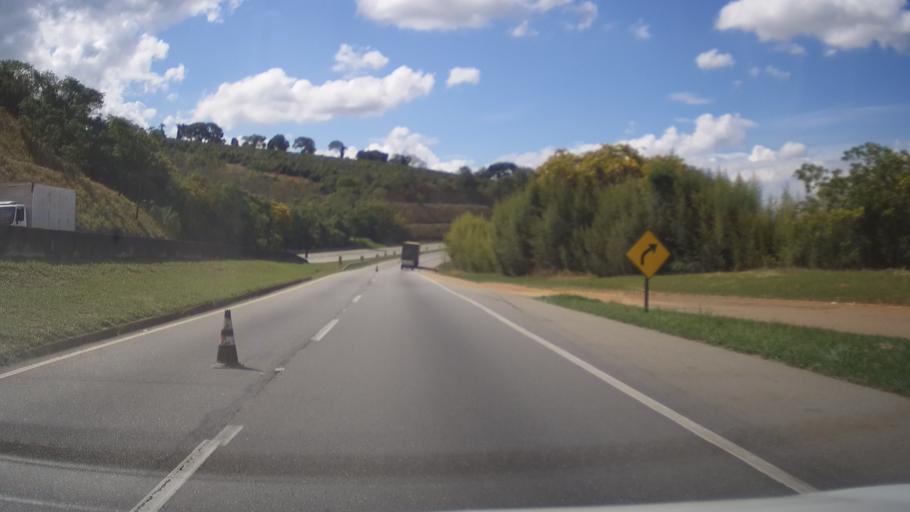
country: BR
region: Minas Gerais
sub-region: Oliveira
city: Oliveira
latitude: -20.8362
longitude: -44.8243
